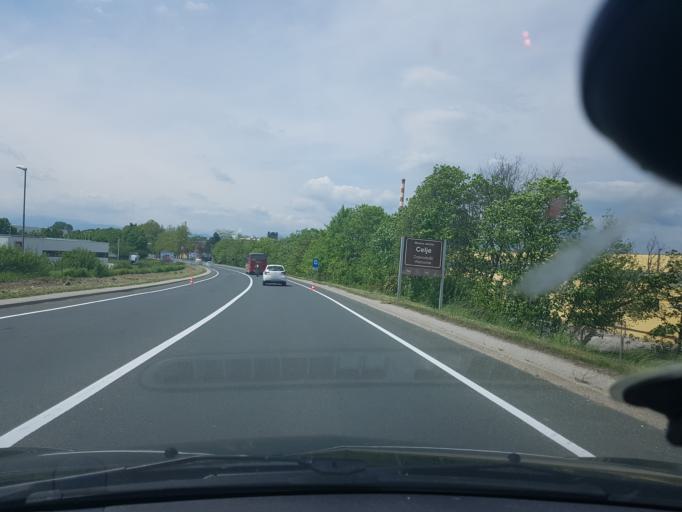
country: SI
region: Store
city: Store
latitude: 46.2339
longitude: 15.2992
